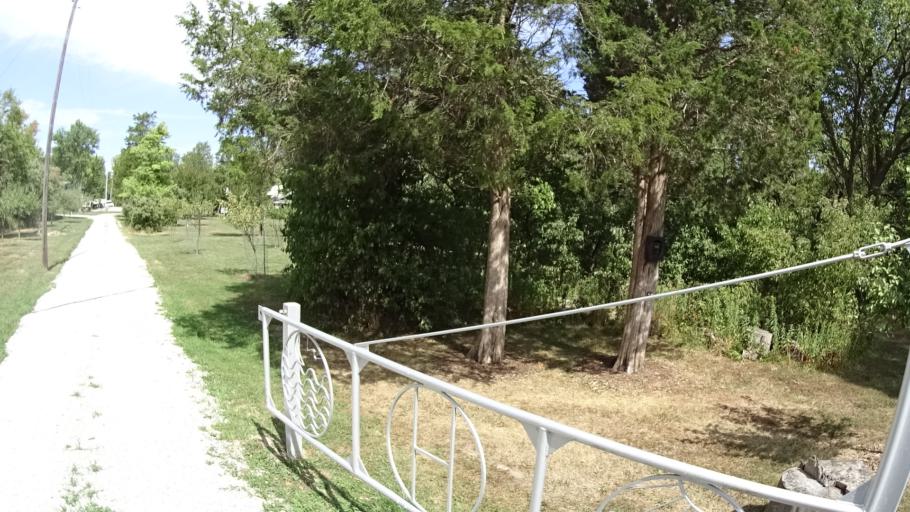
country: US
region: Ohio
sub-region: Erie County
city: Sandusky
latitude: 41.5978
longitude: -82.6805
